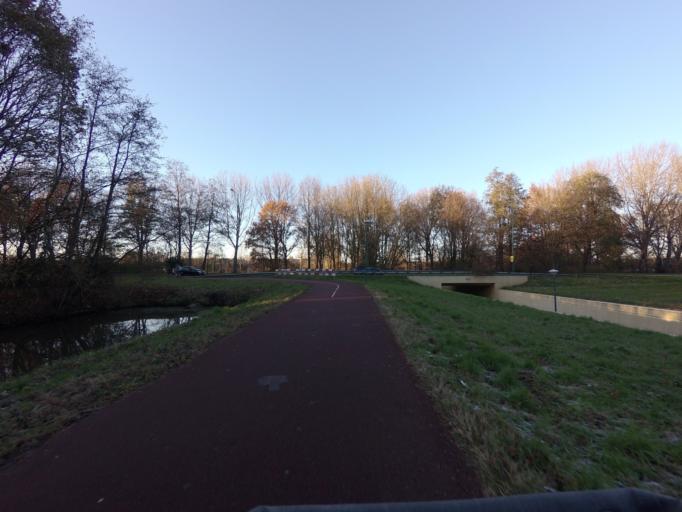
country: NL
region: Utrecht
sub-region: Stichtse Vecht
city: Spechtenkamp
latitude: 52.1270
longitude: 5.0263
